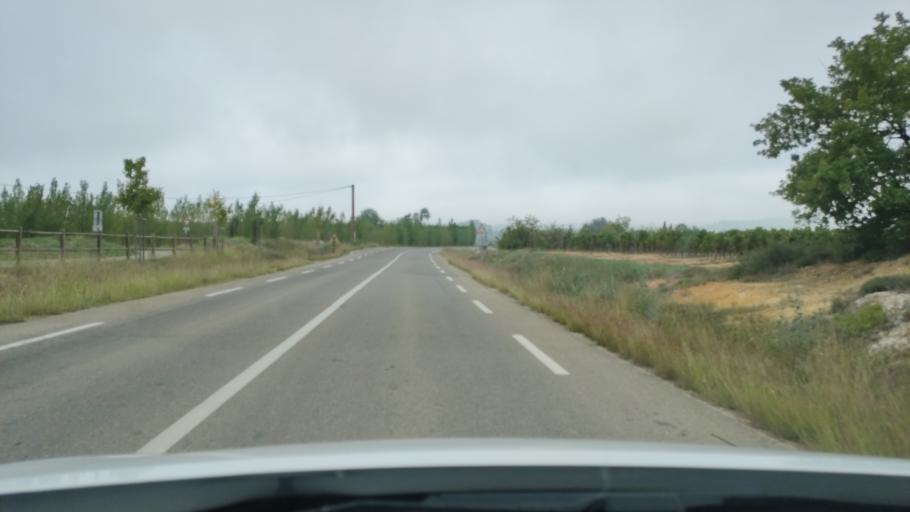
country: FR
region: Provence-Alpes-Cote d'Azur
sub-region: Departement du Vaucluse
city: Bonnieux
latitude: 43.8635
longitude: 5.3068
